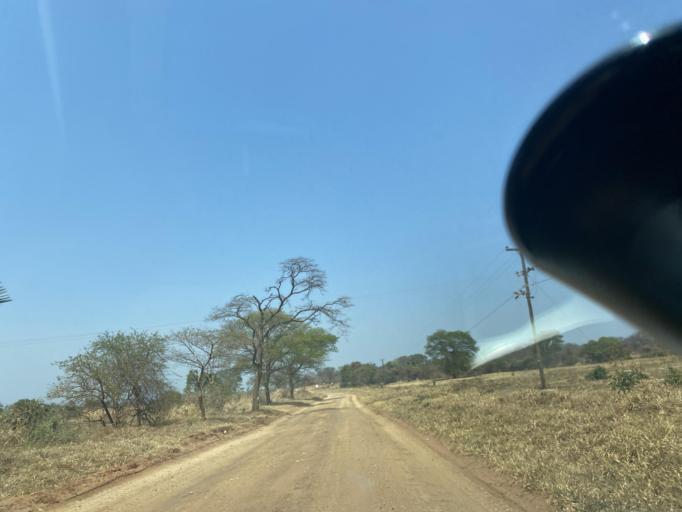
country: ZM
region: Lusaka
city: Kafue
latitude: -15.5435
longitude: 28.0731
